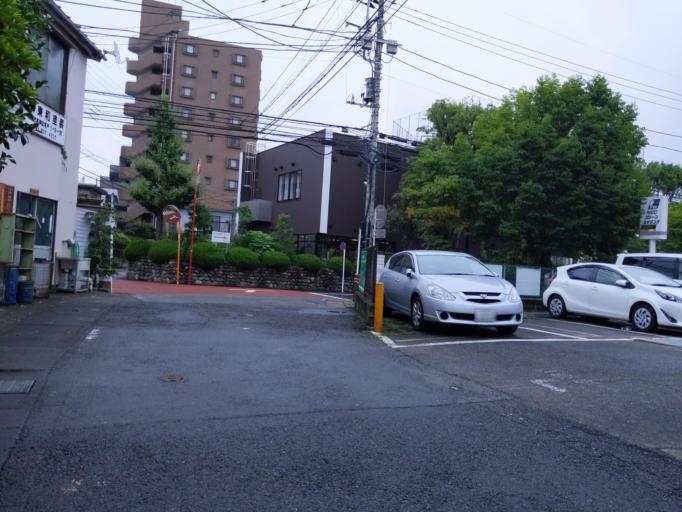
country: JP
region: Tokyo
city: Chofugaoka
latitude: 35.5983
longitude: 139.6194
